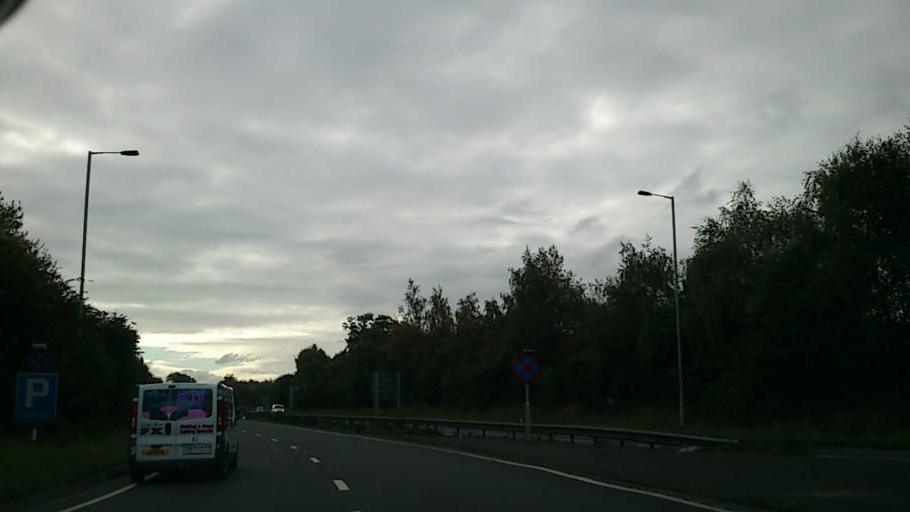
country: GB
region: England
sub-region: Shropshire
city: Great Hanwood
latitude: 52.7026
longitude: -2.8096
